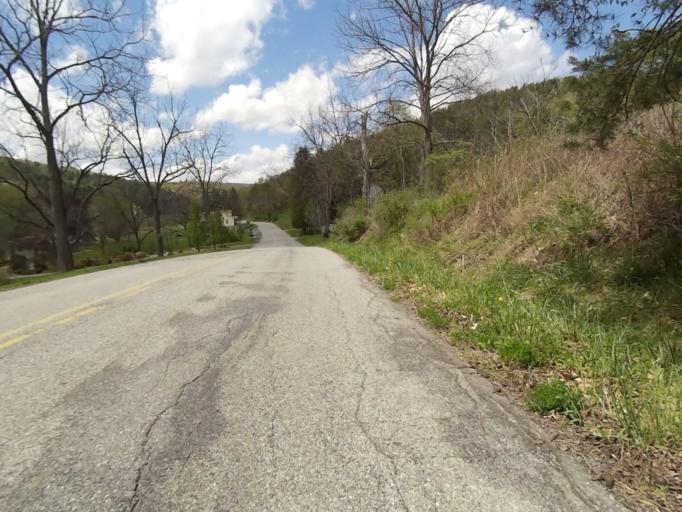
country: US
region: Pennsylvania
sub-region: Centre County
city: Milesburg
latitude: 40.9250
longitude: -77.8691
